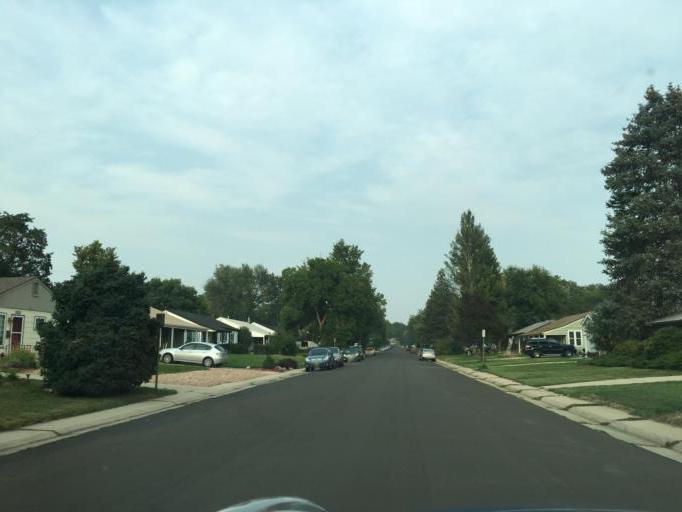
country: US
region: Colorado
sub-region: Arapahoe County
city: Glendale
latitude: 39.6835
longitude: -104.9367
